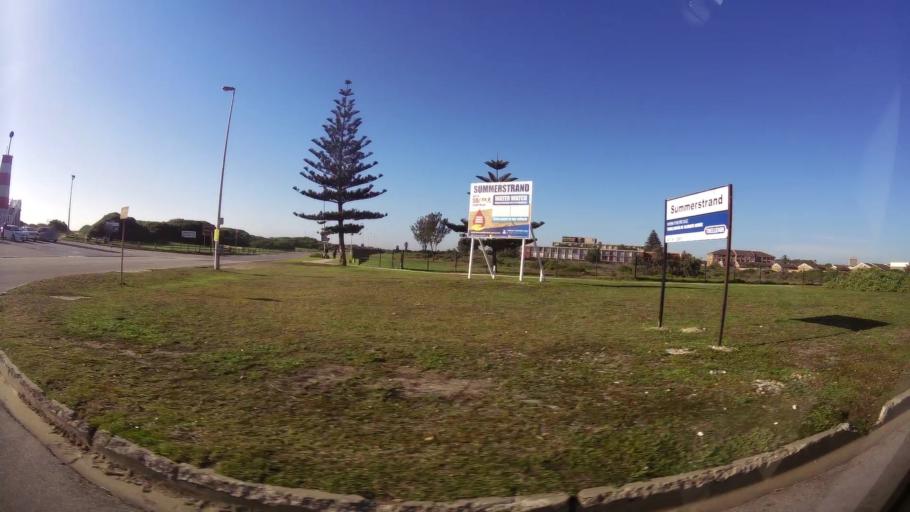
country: ZA
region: Eastern Cape
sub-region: Nelson Mandela Bay Metropolitan Municipality
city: Port Elizabeth
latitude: -33.9914
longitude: 25.6753
